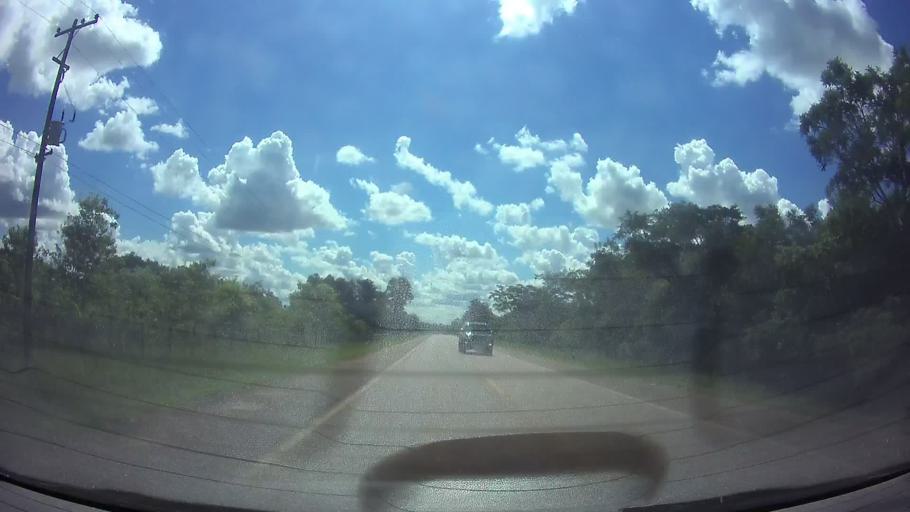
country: PY
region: Paraguari
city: La Colmena
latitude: -25.9019
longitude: -56.7782
